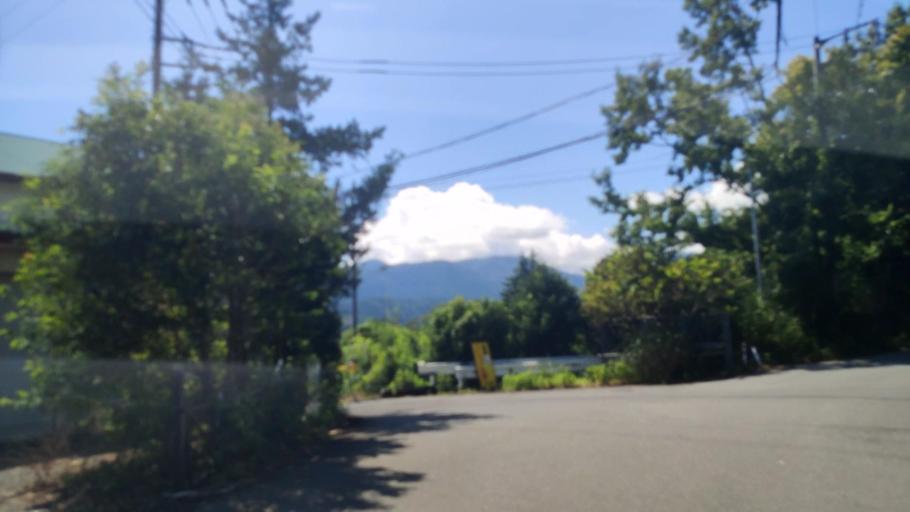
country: JP
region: Kanagawa
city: Odawara
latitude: 35.2516
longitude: 139.1334
